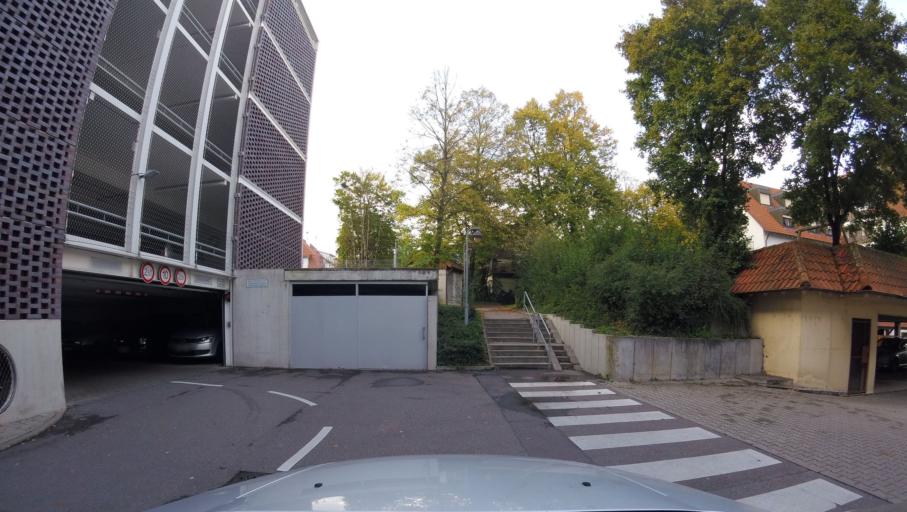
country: DE
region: Baden-Wuerttemberg
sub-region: Regierungsbezirk Stuttgart
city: Backnang
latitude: 48.9456
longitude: 9.4265
